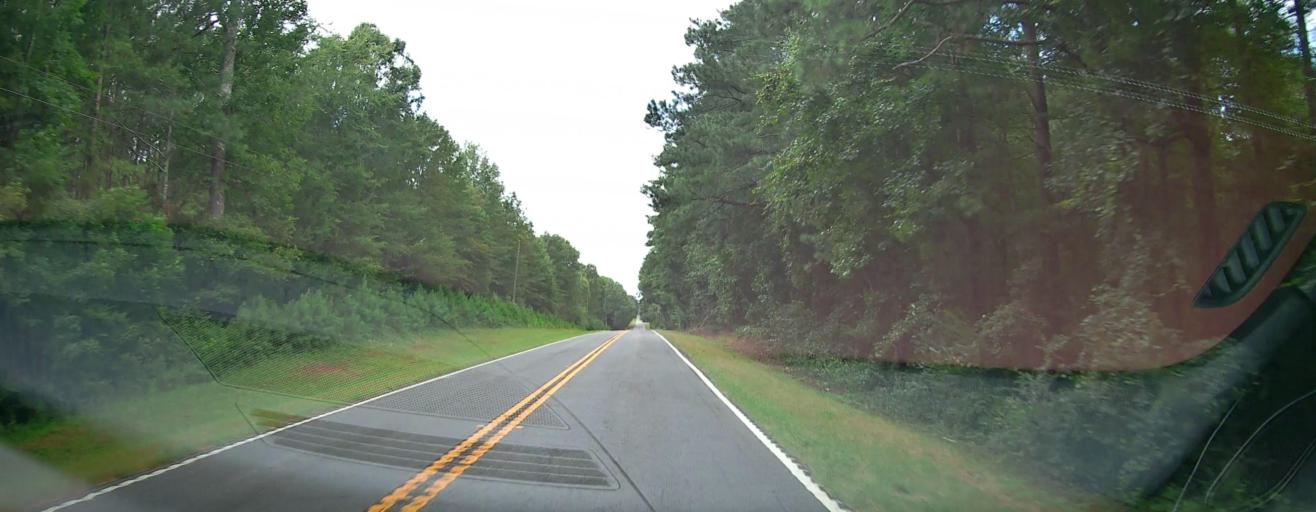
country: US
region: Georgia
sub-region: Dooly County
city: Unadilla
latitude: 32.2911
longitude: -83.8612
